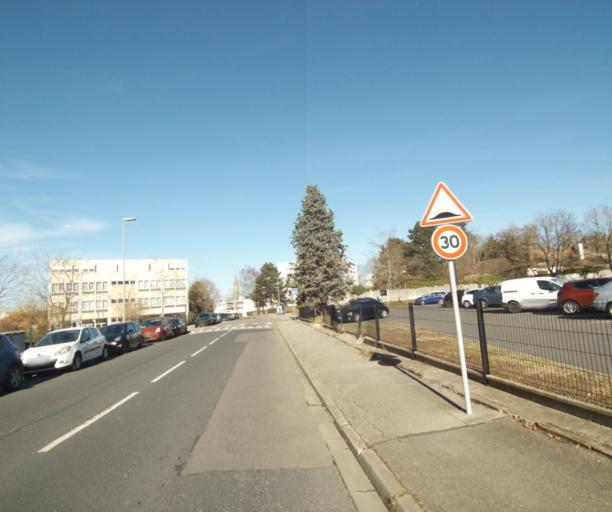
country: FR
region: Lorraine
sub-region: Departement de Meurthe-et-Moselle
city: Villers-les-Nancy
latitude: 48.6676
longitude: 6.1716
